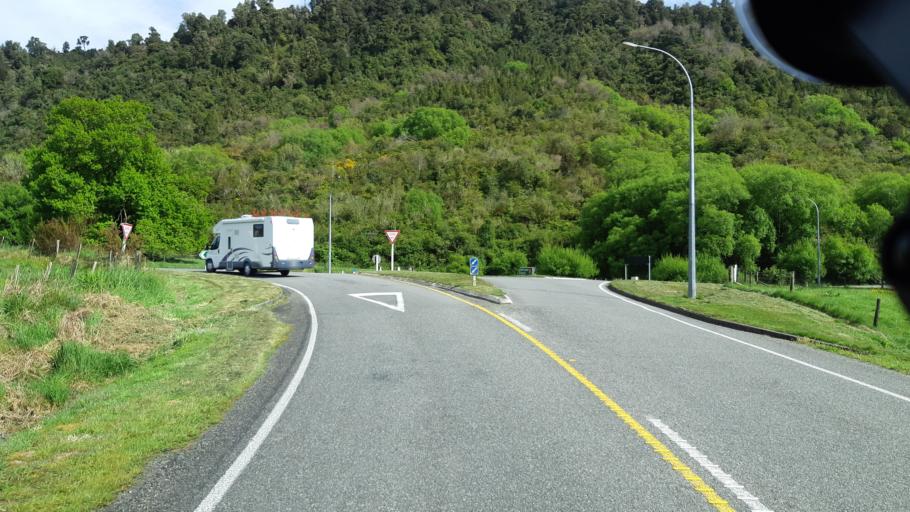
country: NZ
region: West Coast
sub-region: Buller District
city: Westport
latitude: -41.8582
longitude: 171.9377
